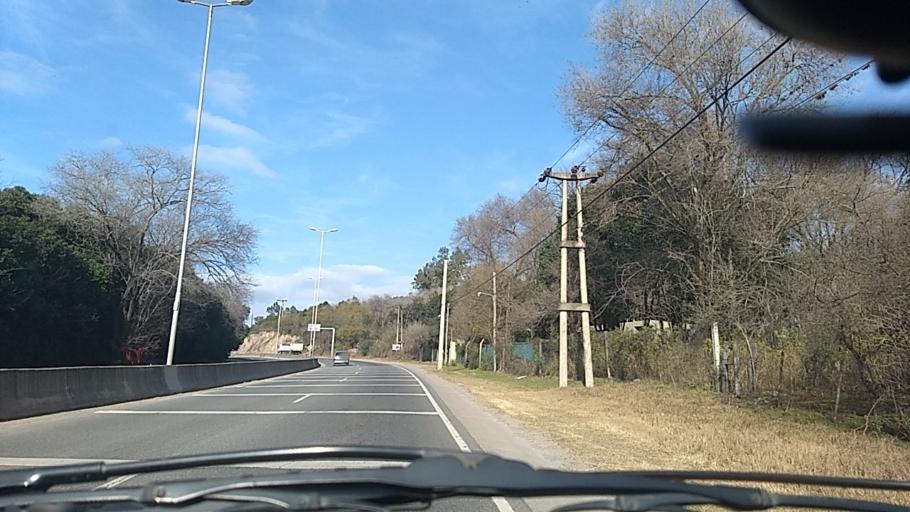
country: AR
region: Cordoba
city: Salsipuedes
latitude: -31.1565
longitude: -64.3006
